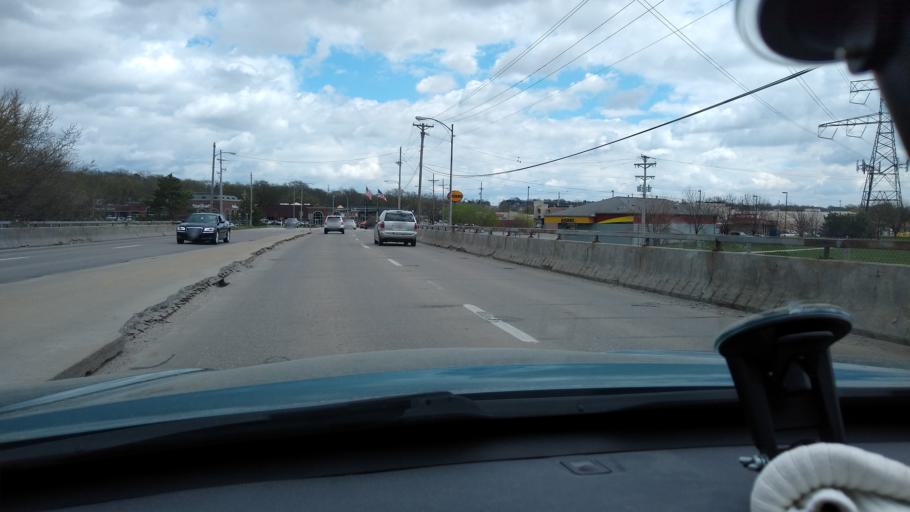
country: US
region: Nebraska
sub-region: Douglas County
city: Ralston
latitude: 41.2339
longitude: -96.0557
